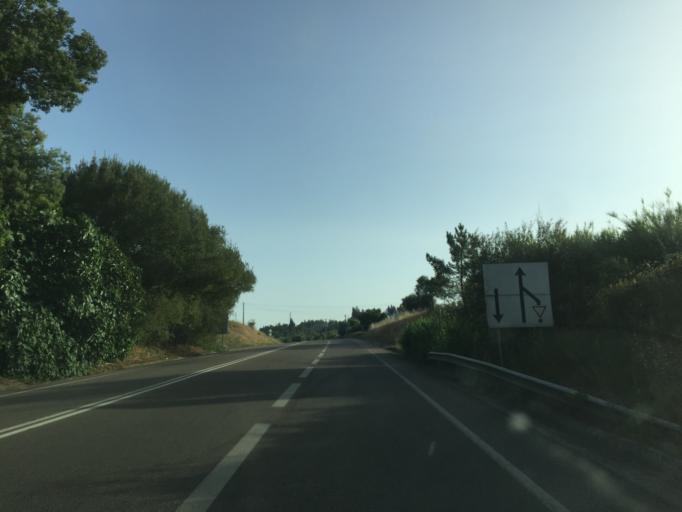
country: PT
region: Santarem
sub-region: Tomar
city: Tomar
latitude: 39.5283
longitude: -8.4063
